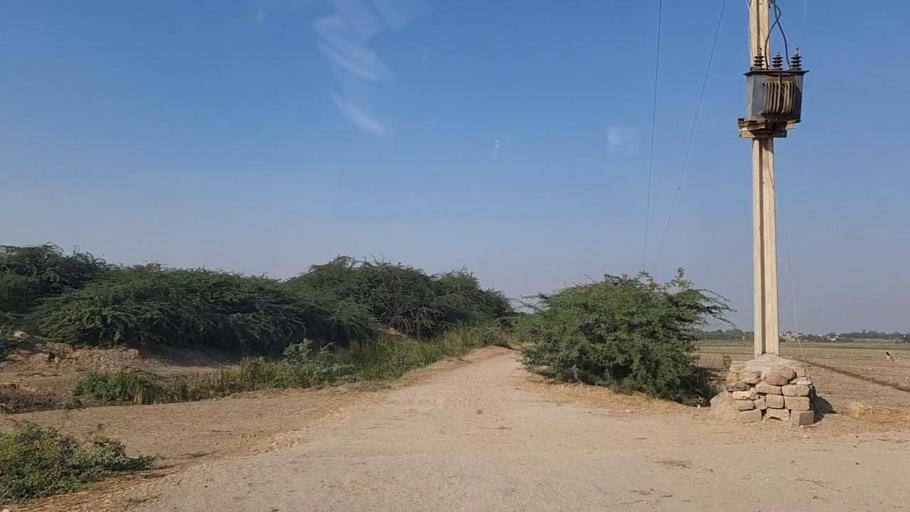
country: PK
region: Sindh
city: Thatta
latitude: 24.7610
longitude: 67.9638
